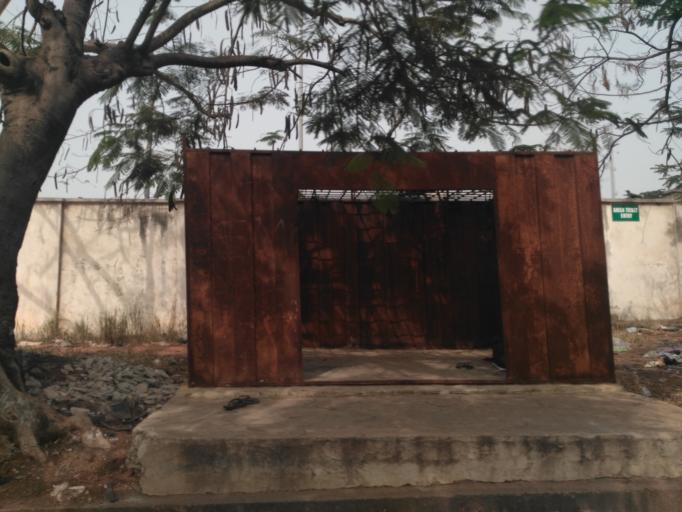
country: GH
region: Ashanti
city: Kumasi
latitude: 6.6810
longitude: -1.6057
